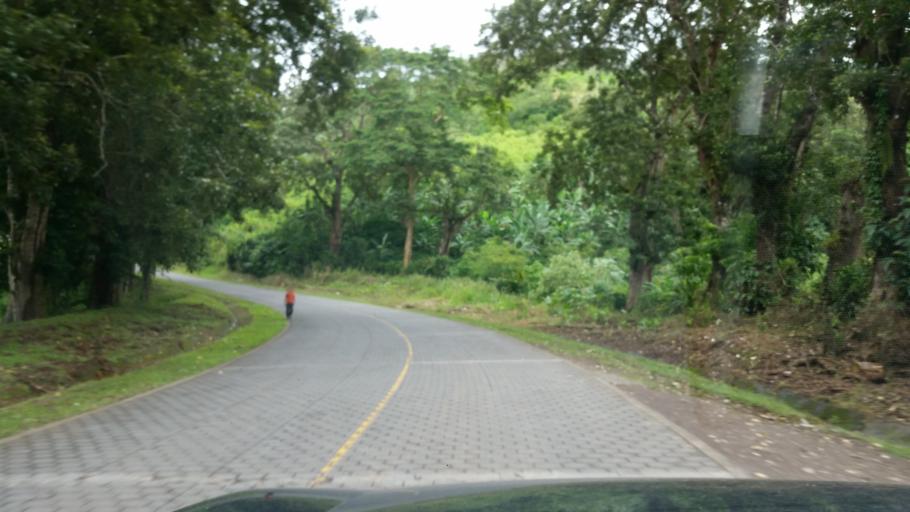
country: NI
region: Jinotega
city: Jinotega
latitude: 13.1997
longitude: -85.7309
